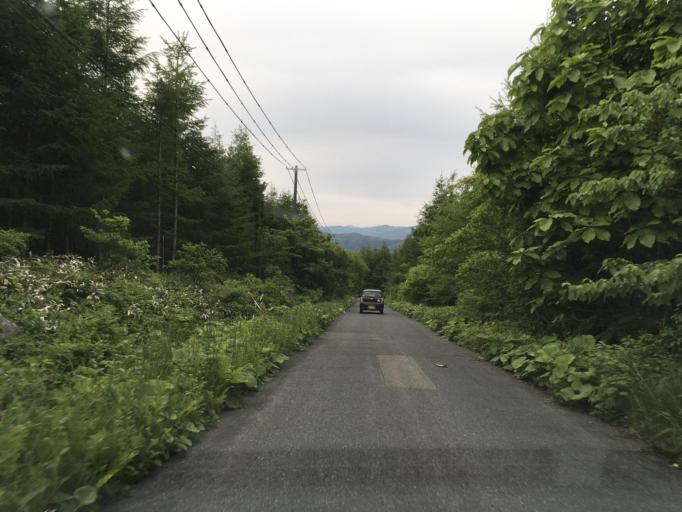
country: JP
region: Iwate
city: Mizusawa
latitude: 39.1420
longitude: 141.3052
